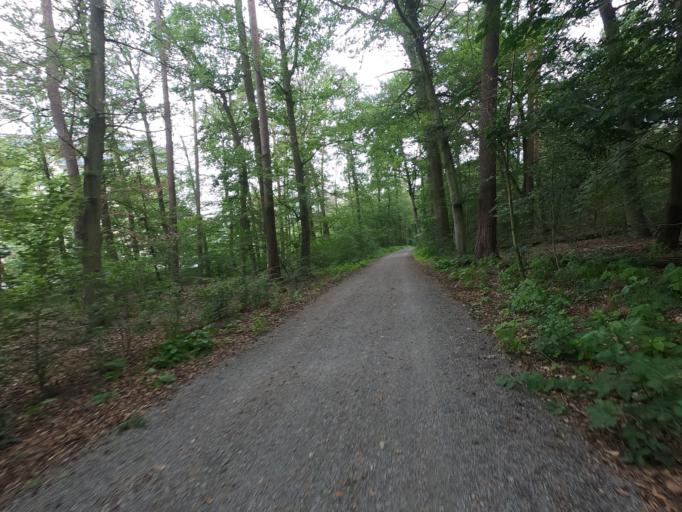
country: DE
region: Hesse
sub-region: Regierungsbezirk Darmstadt
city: Offenbach
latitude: 50.0628
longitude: 8.7500
